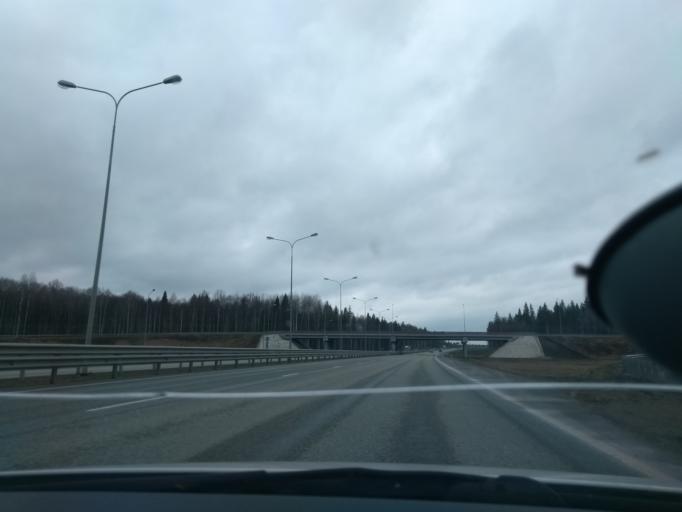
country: RU
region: Perm
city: Bershet'
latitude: 57.6978
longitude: 56.3835
